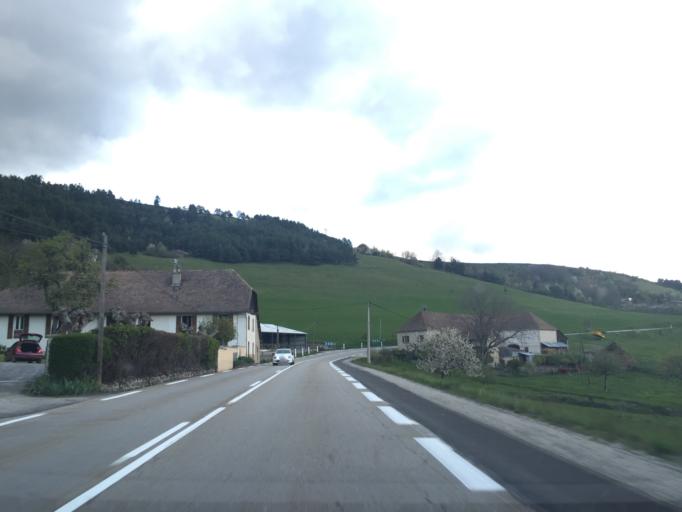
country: FR
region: Rhone-Alpes
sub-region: Departement de l'Isere
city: La Motte-Saint-Martin
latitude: 44.8991
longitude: 5.6150
